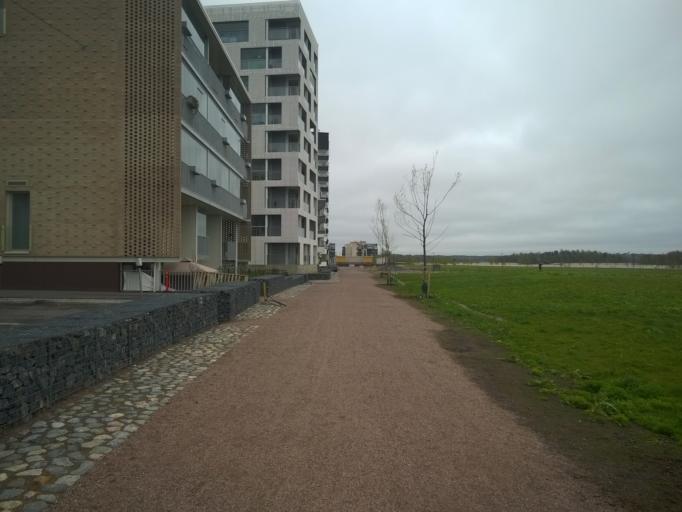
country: FI
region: Uusimaa
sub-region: Helsinki
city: Helsinki
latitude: 60.2026
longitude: 24.9731
